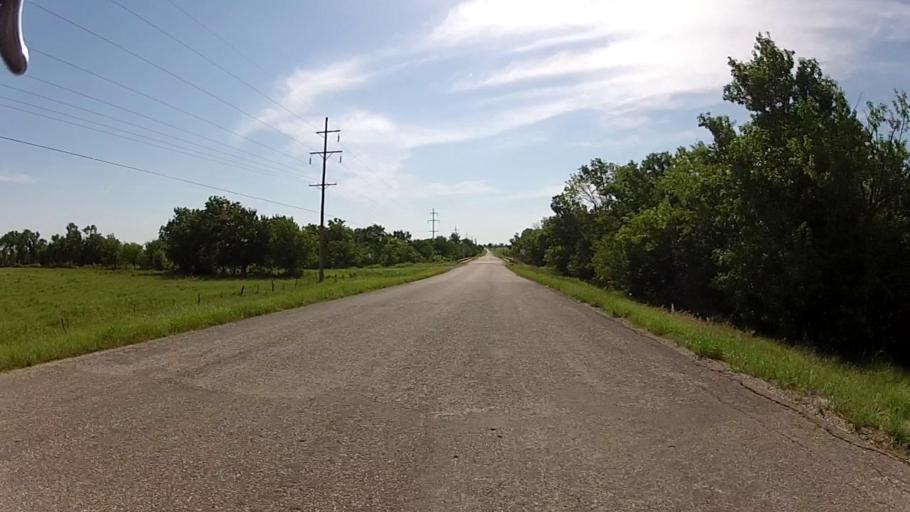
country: US
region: Kansas
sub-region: Cowley County
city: Winfield
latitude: 37.0710
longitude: -96.6670
